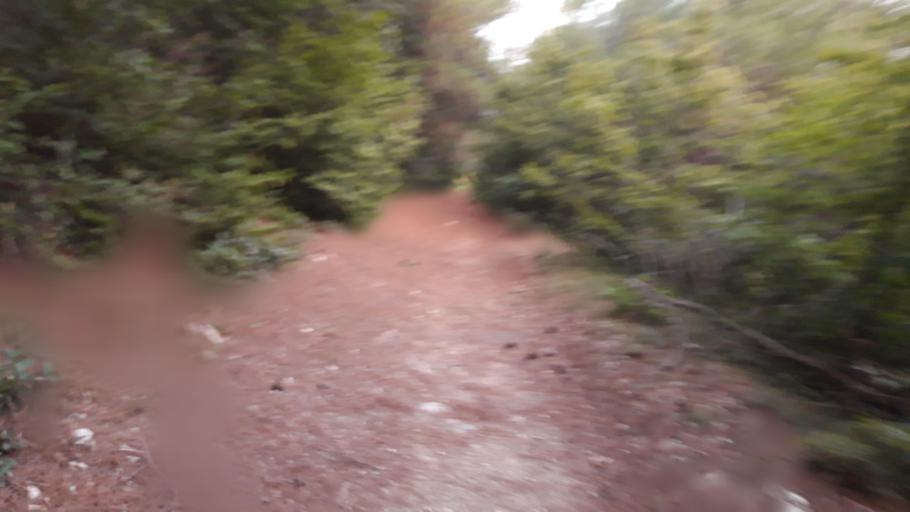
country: RU
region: Krasnodarskiy
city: Gelendzhik
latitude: 44.5799
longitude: 38.0848
